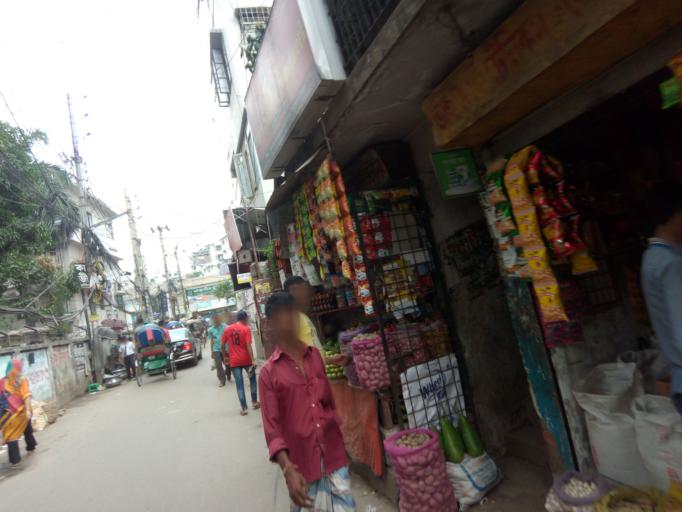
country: BD
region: Dhaka
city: Azimpur
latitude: 23.7537
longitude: 90.3877
